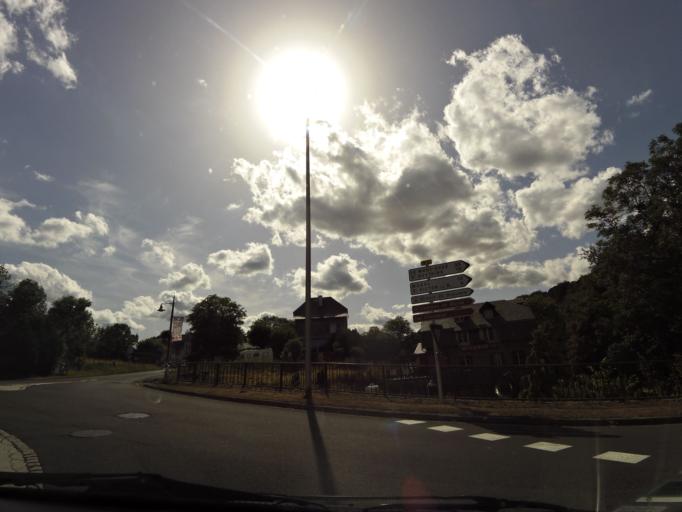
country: FR
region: Auvergne
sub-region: Departement du Puy-de-Dome
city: Mont-Dore
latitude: 45.5155
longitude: 2.9389
